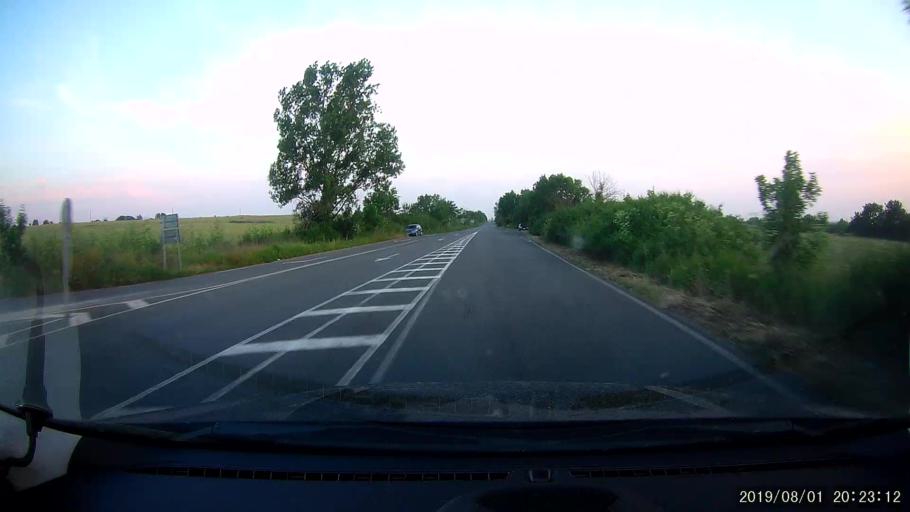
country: BG
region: Yambol
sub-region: Obshtina Elkhovo
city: Elkhovo
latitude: 42.2534
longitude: 26.5987
